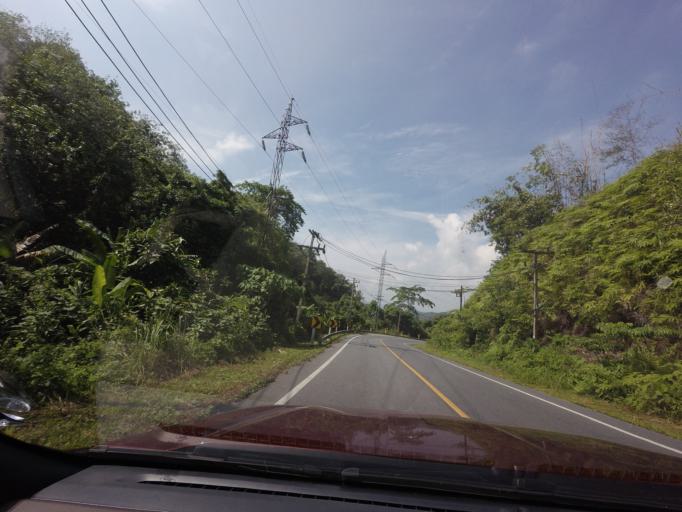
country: TH
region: Yala
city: Betong
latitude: 5.8364
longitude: 101.1194
